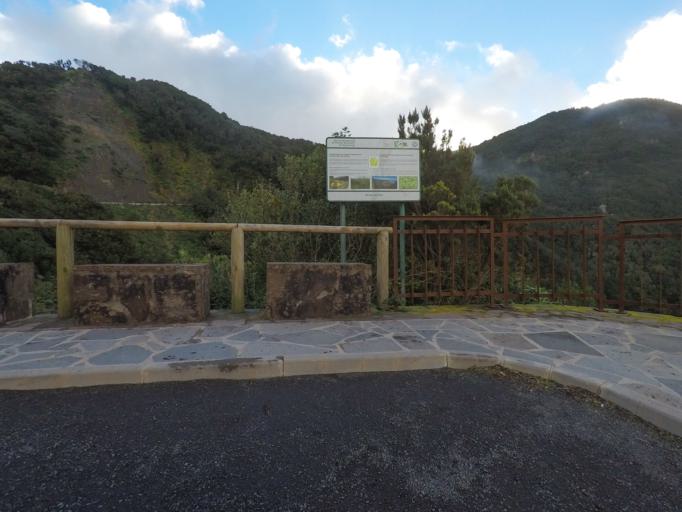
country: ES
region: Canary Islands
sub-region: Provincia de Santa Cruz de Tenerife
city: Hermigua
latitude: 28.1251
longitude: -17.2088
